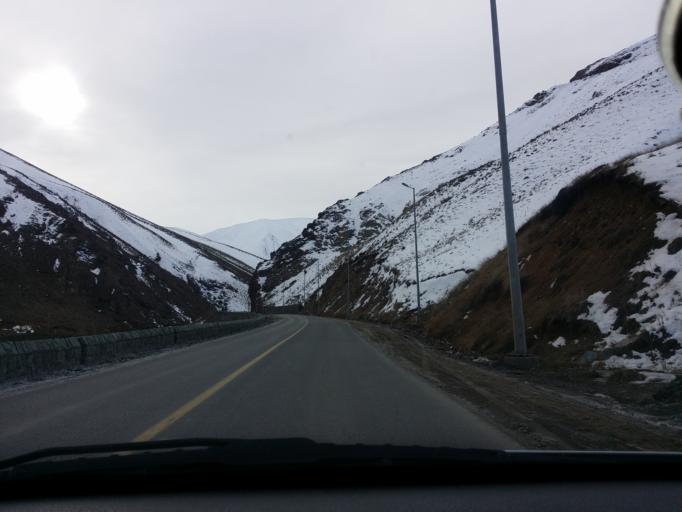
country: IR
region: Tehran
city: Tajrish
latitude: 36.1721
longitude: 51.3149
